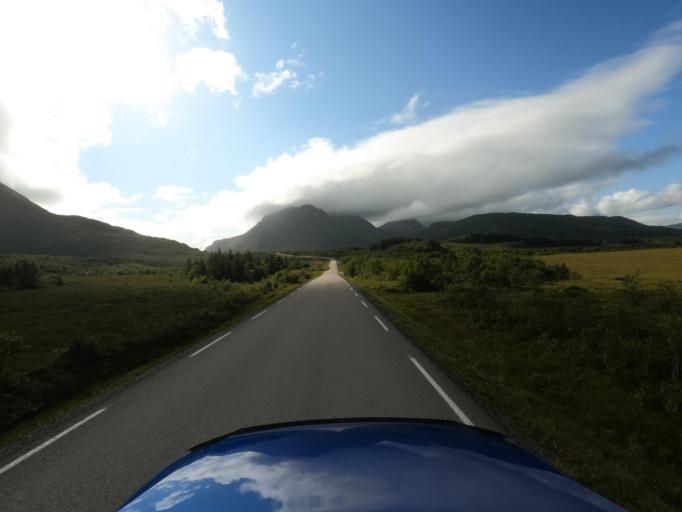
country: NO
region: Nordland
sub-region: Vagan
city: Kabelvag
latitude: 68.2875
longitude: 14.1631
